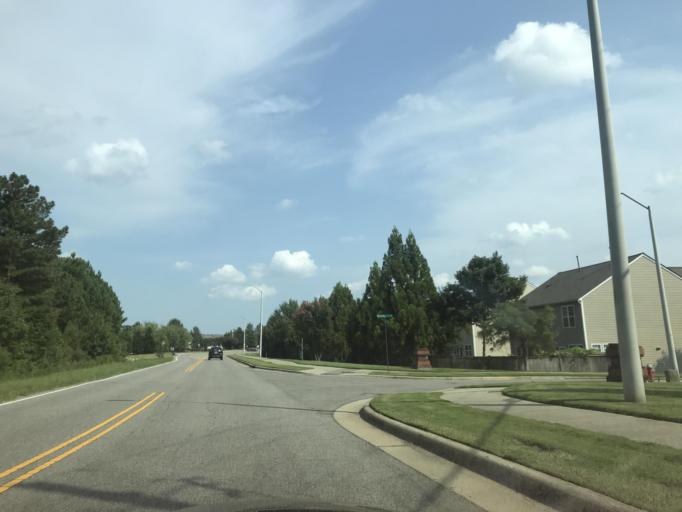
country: US
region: North Carolina
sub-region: Wake County
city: Morrisville
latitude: 35.8373
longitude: -78.8647
